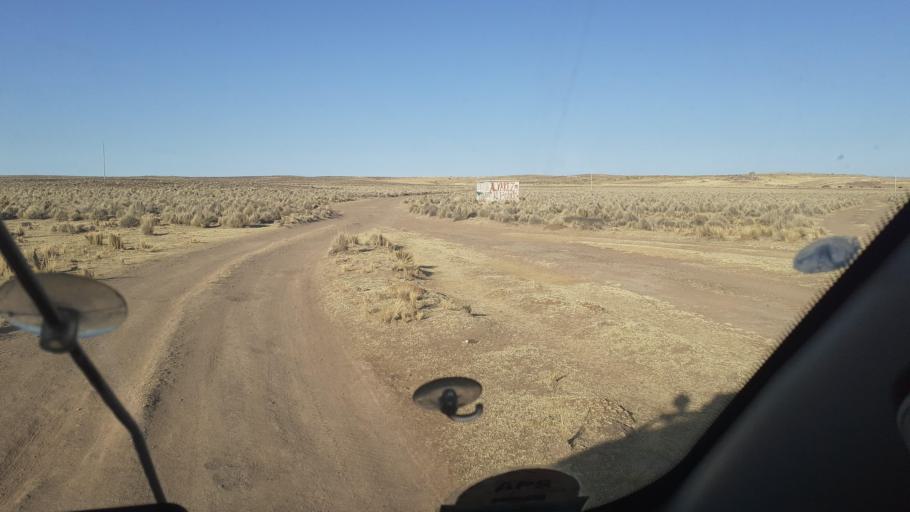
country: BO
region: La Paz
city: Tiahuanaco
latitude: -17.0018
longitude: -68.7279
